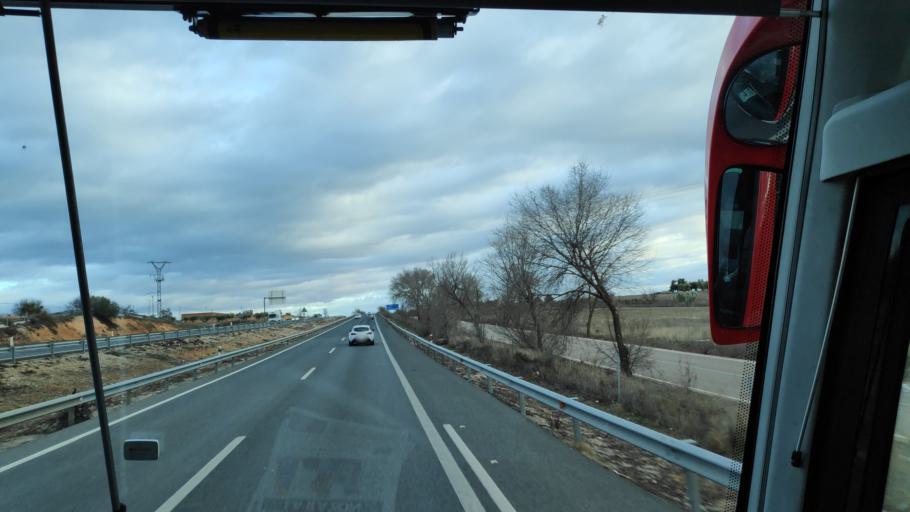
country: ES
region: Madrid
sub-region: Provincia de Madrid
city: Villarejo de Salvanes
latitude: 40.1609
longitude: -3.2636
